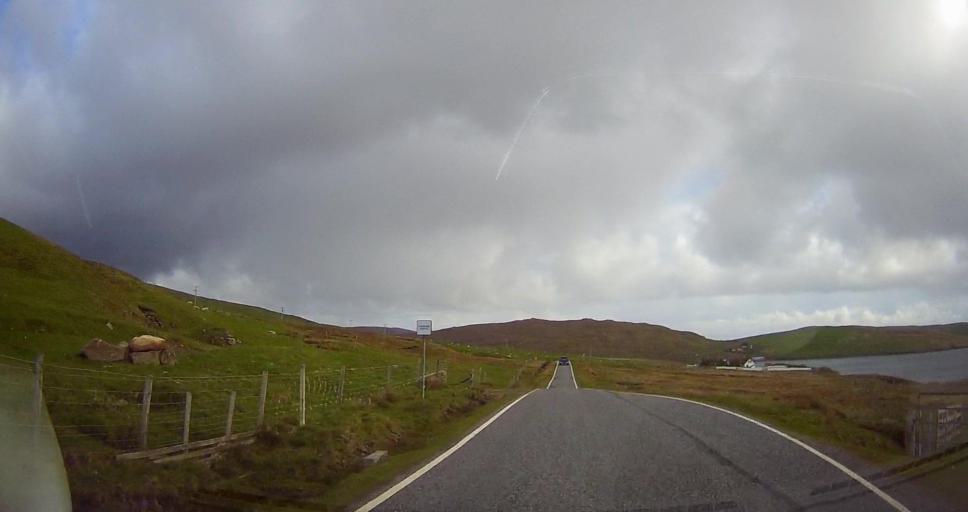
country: GB
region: Scotland
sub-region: Shetland Islands
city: Lerwick
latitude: 60.5326
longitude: -1.3618
